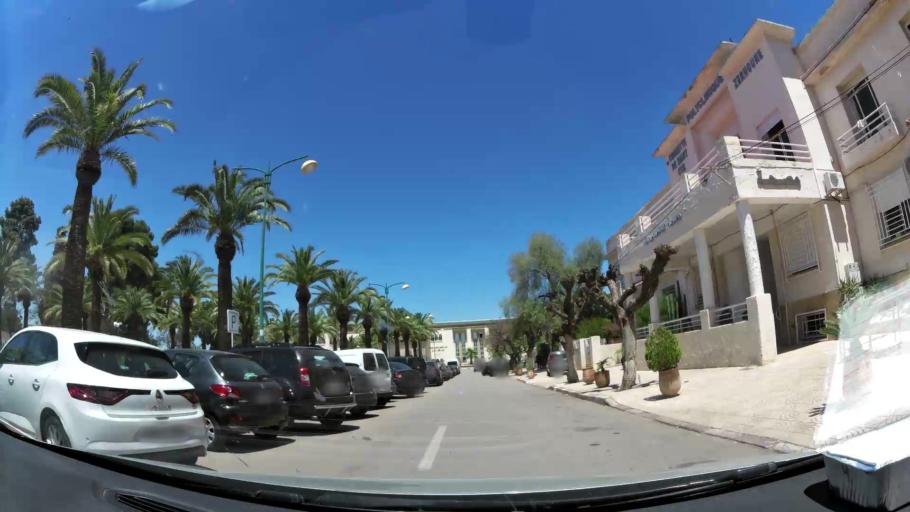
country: MA
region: Meknes-Tafilalet
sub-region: Meknes
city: Meknes
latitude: 33.9054
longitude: -5.5524
